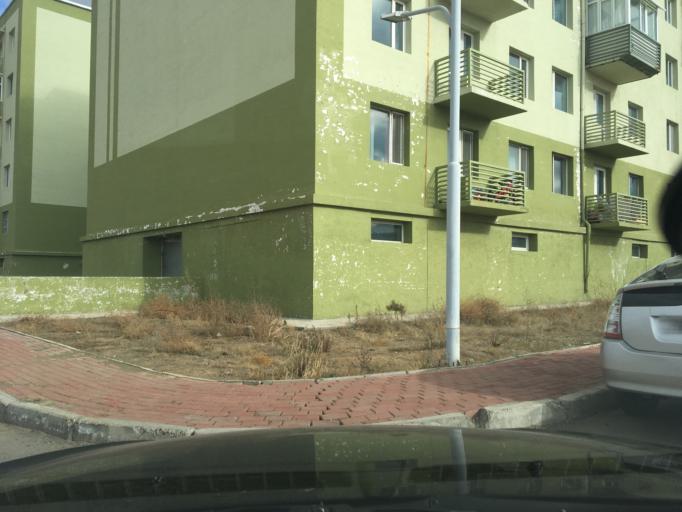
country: MN
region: Ulaanbaatar
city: Ulaanbaatar
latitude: 47.8786
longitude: 106.8450
